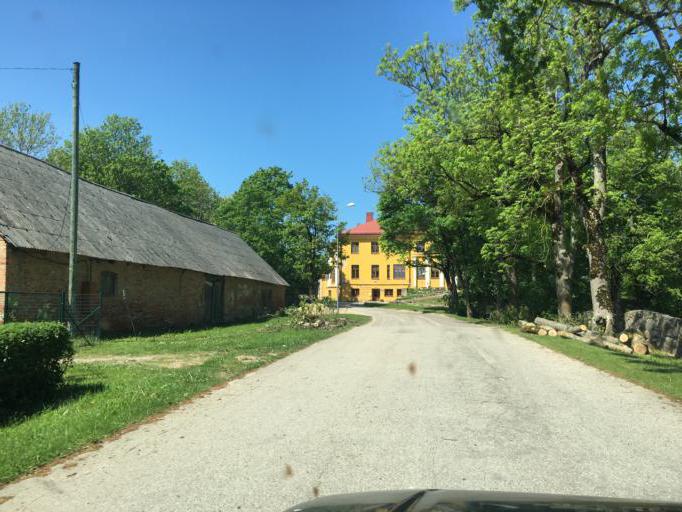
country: LV
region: Talsu Rajons
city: Valdemarpils
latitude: 57.4490
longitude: 22.5270
